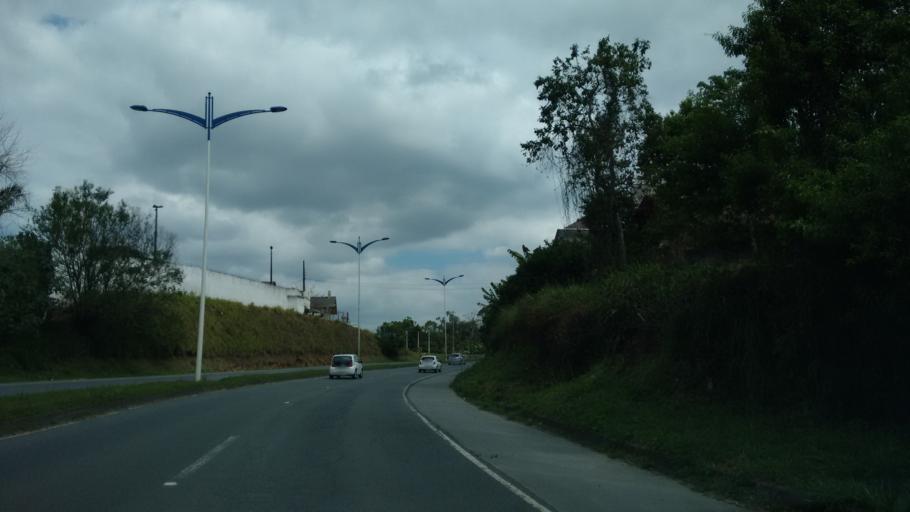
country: BR
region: Santa Catarina
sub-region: Blumenau
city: Blumenau
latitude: -26.8752
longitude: -49.0673
